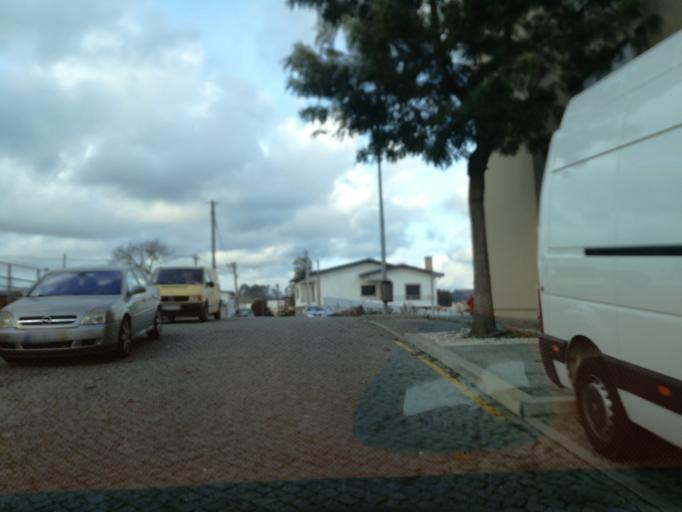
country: PT
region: Porto
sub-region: Maia
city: Nogueira
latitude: 41.2540
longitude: -8.6006
